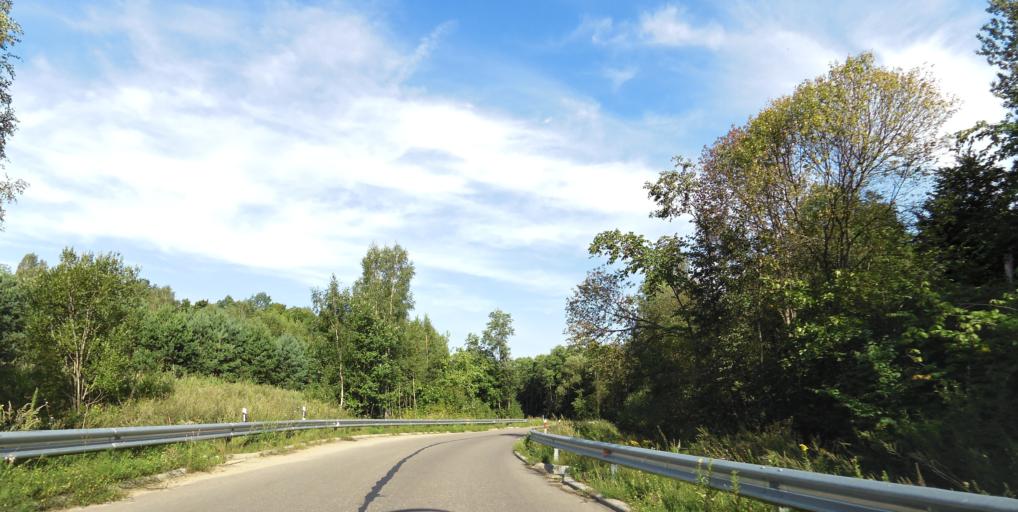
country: LT
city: Grigiskes
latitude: 54.7268
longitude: 25.0707
